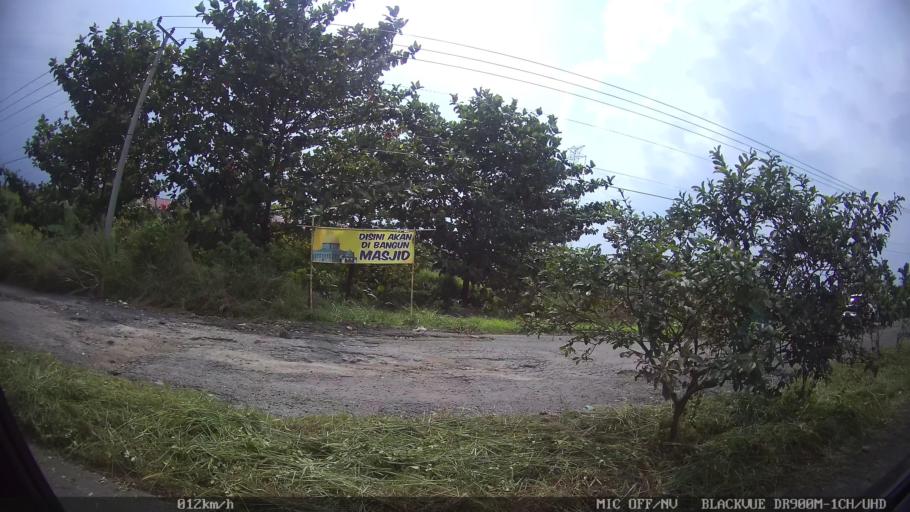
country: ID
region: Lampung
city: Bandarlampung
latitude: -5.4110
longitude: 105.1977
